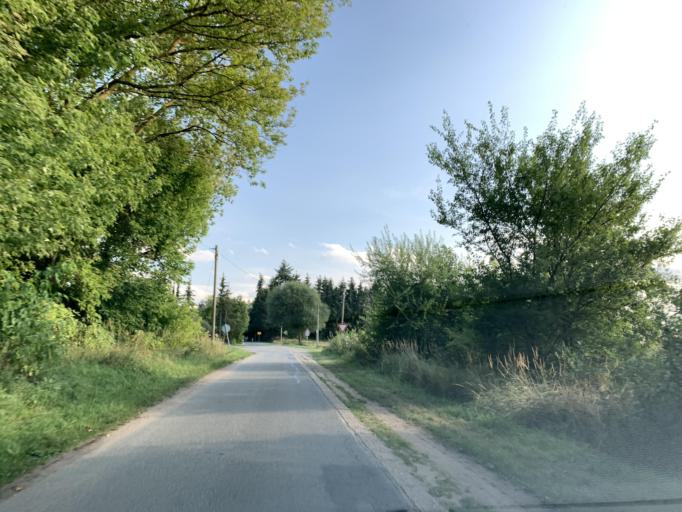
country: DE
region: Mecklenburg-Vorpommern
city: Loitz
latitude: 53.3568
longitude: 13.3525
